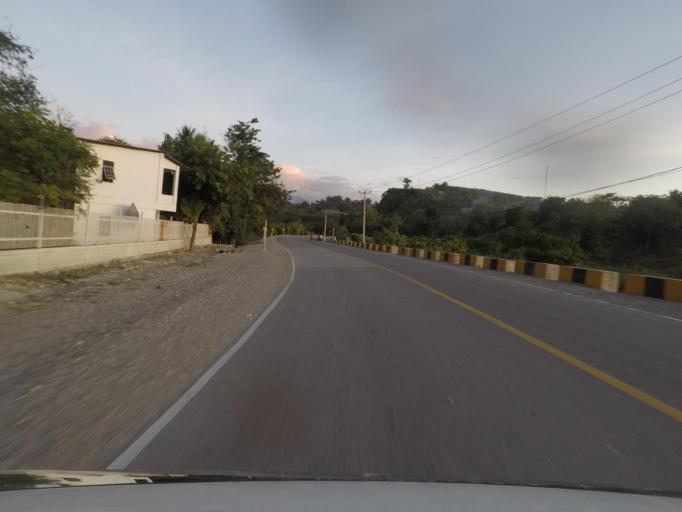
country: TL
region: Baucau
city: Baucau
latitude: -8.4700
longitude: 126.6028
